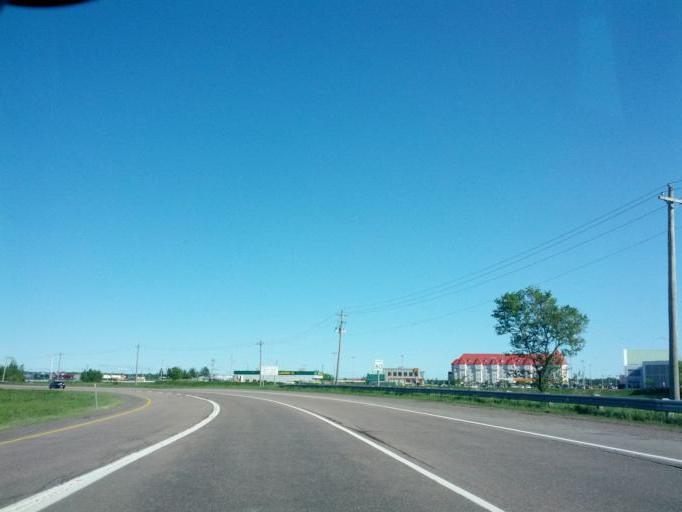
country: CA
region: New Brunswick
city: Moncton
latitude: 46.0964
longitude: -64.7691
